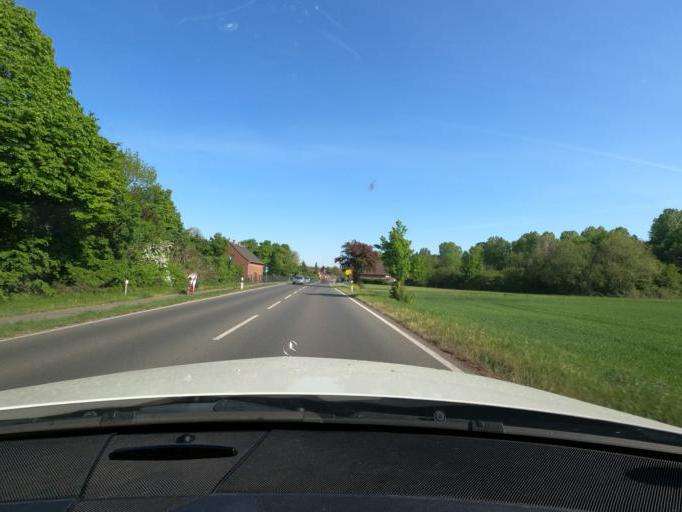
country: DE
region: North Rhine-Westphalia
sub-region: Regierungsbezirk Dusseldorf
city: Moers
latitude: 51.4798
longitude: 6.6011
